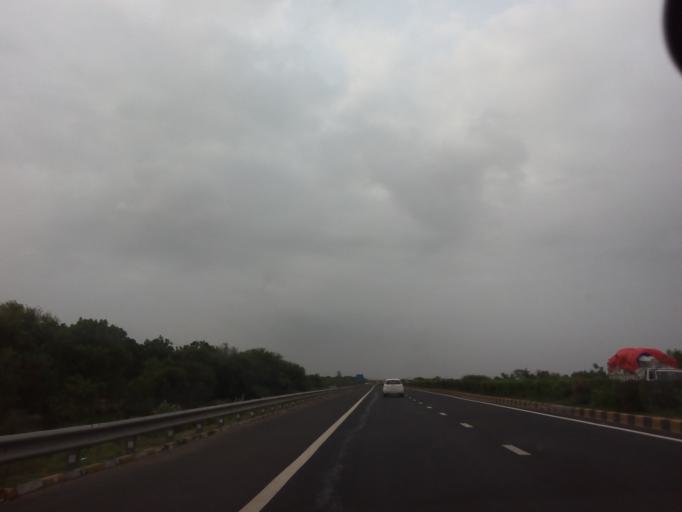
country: IN
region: Gujarat
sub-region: Kheda
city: Mahemdavad
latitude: 22.8743
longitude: 72.8006
